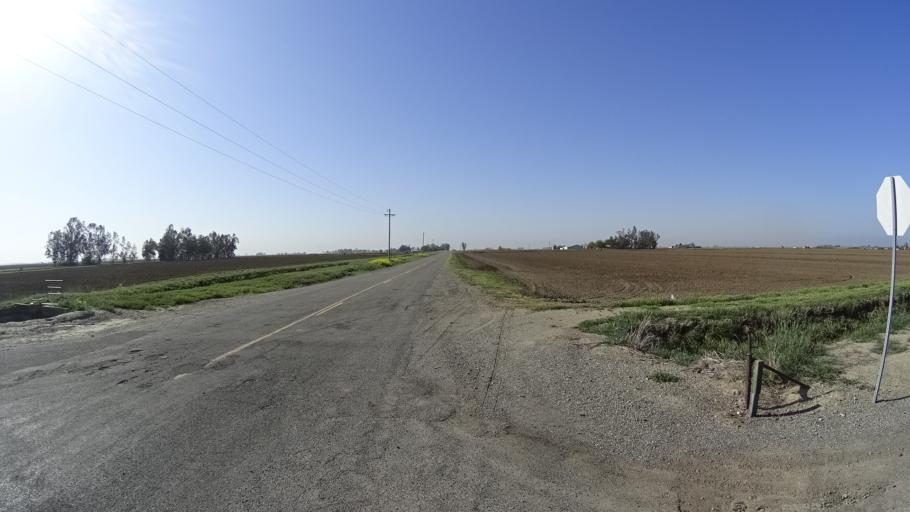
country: US
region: California
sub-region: Glenn County
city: Willows
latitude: 39.5749
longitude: -122.1078
